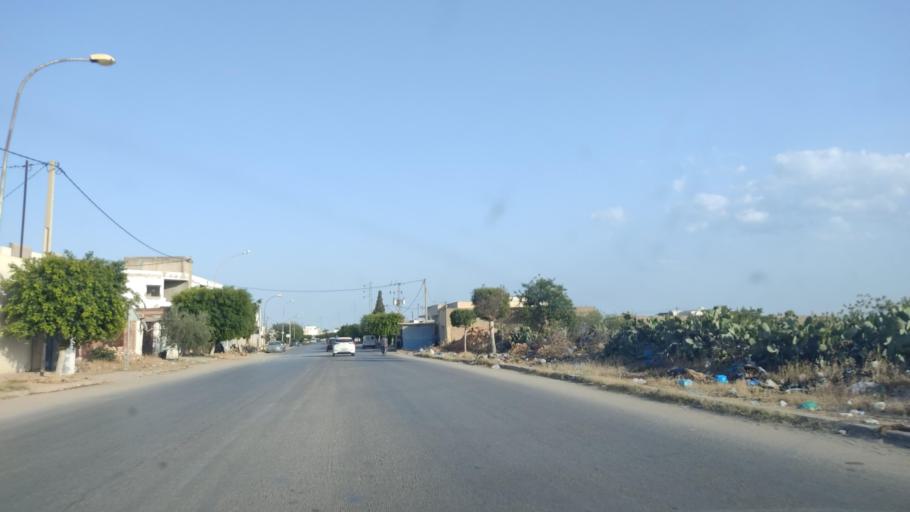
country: TN
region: Safaqis
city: Sfax
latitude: 34.7888
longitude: 10.6890
